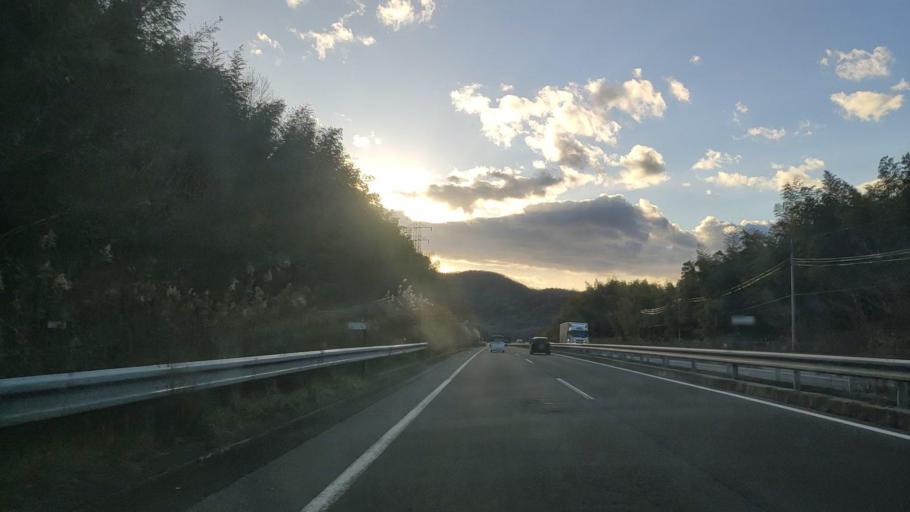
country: JP
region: Hyogo
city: Tatsunocho-tominaga
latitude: 34.8592
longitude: 134.6145
